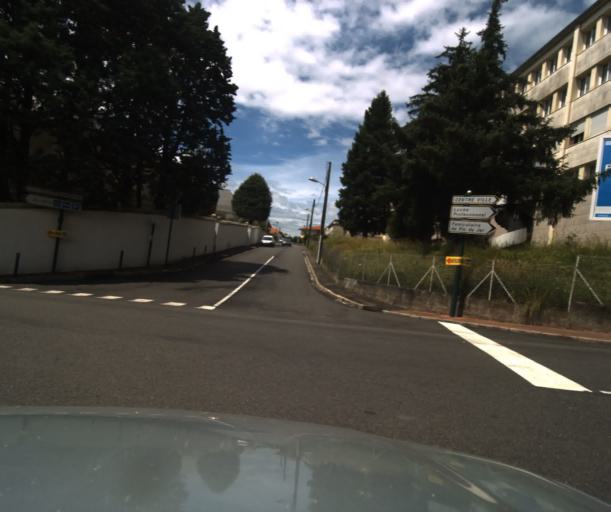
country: FR
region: Midi-Pyrenees
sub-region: Departement des Hautes-Pyrenees
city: Lourdes
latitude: 43.0889
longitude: -0.0494
